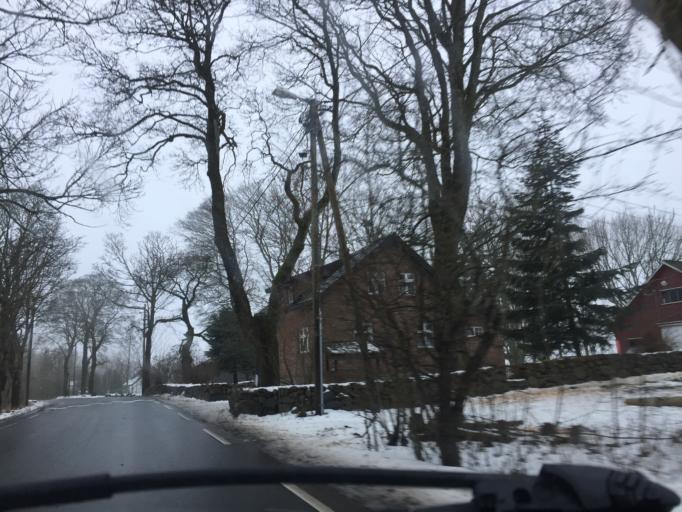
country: NO
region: Akershus
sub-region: As
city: As
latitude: 59.7050
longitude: 10.7650
